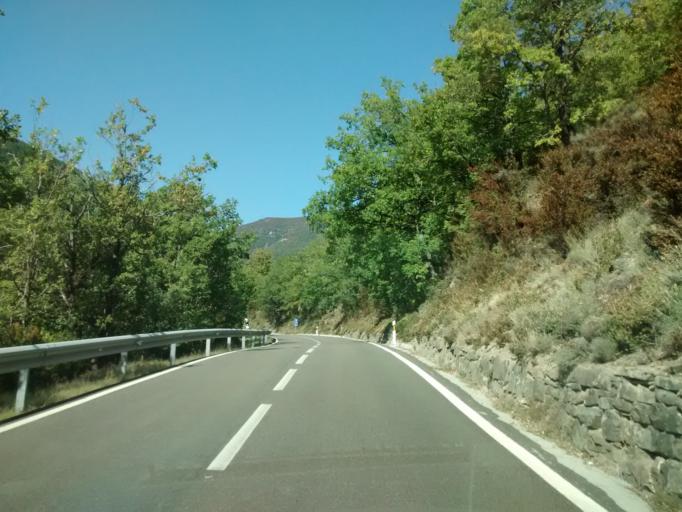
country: ES
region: Aragon
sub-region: Provincia de Huesca
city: Fiscal
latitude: 42.5302
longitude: -0.1364
